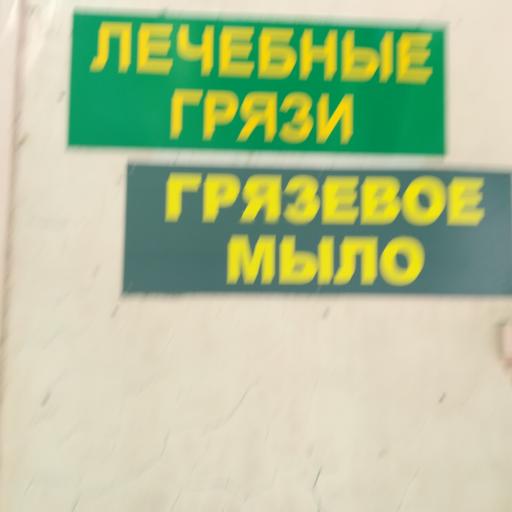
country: RU
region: Krasnodarskiy
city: Anapa
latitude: 44.8937
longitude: 37.3088
